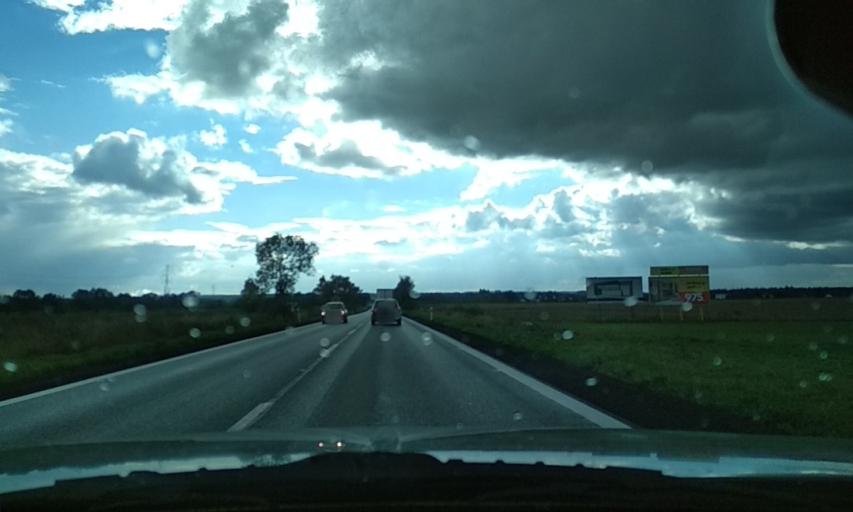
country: PL
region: Silesian Voivodeship
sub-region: Powiat gliwicki
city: Zernica
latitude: 50.2328
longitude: 18.6287
